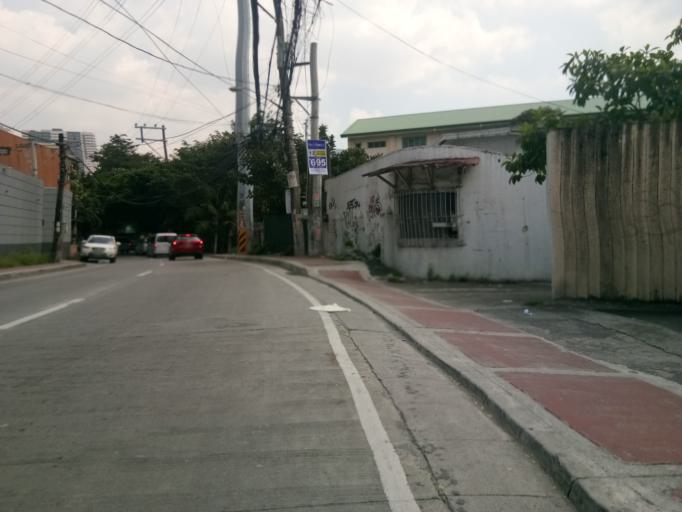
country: PH
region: Metro Manila
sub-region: San Juan
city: San Juan
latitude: 14.6146
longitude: 121.0479
